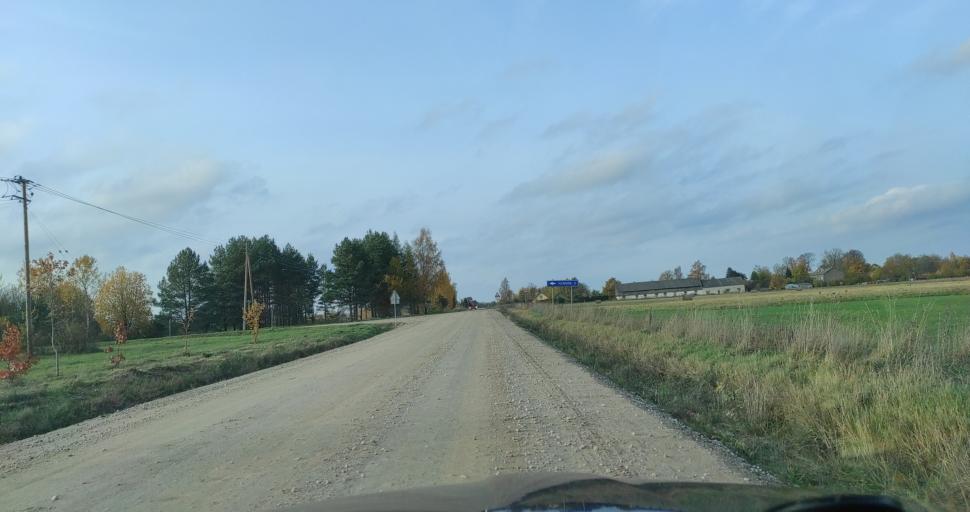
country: LV
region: Vainode
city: Vainode
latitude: 56.4372
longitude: 21.8782
